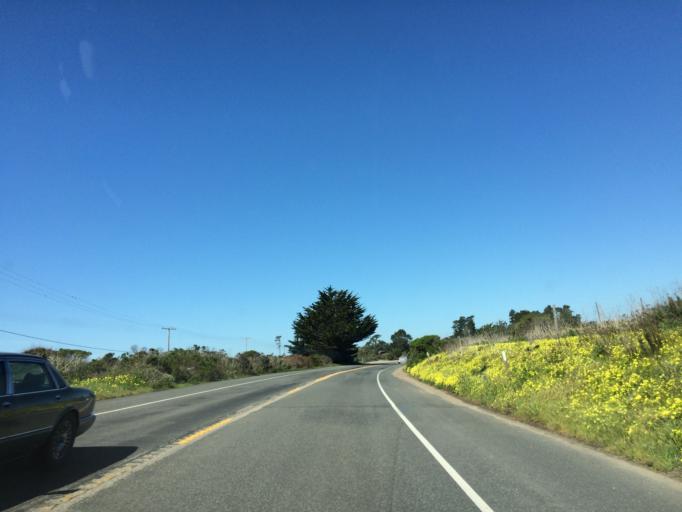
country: US
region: California
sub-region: Santa Cruz County
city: Bonny Doon
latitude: 37.1145
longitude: -122.3016
